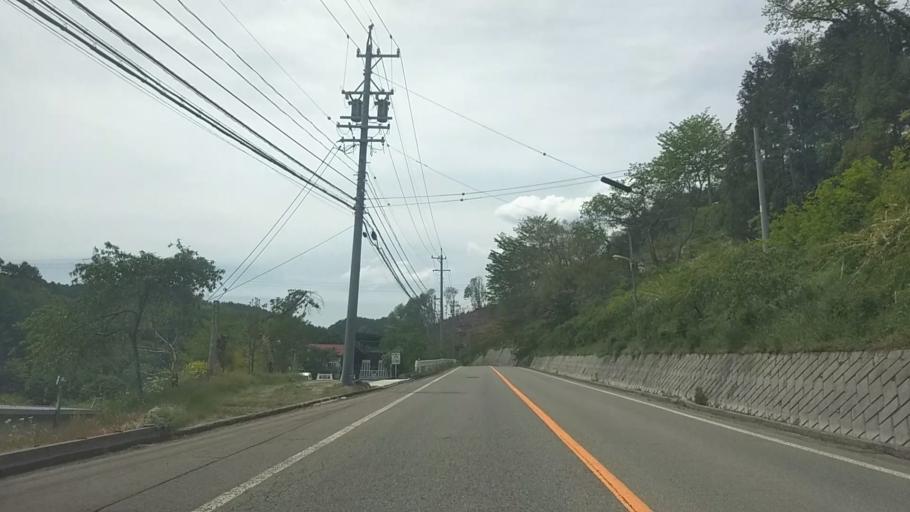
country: JP
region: Nagano
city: Saku
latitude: 36.1225
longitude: 138.4525
